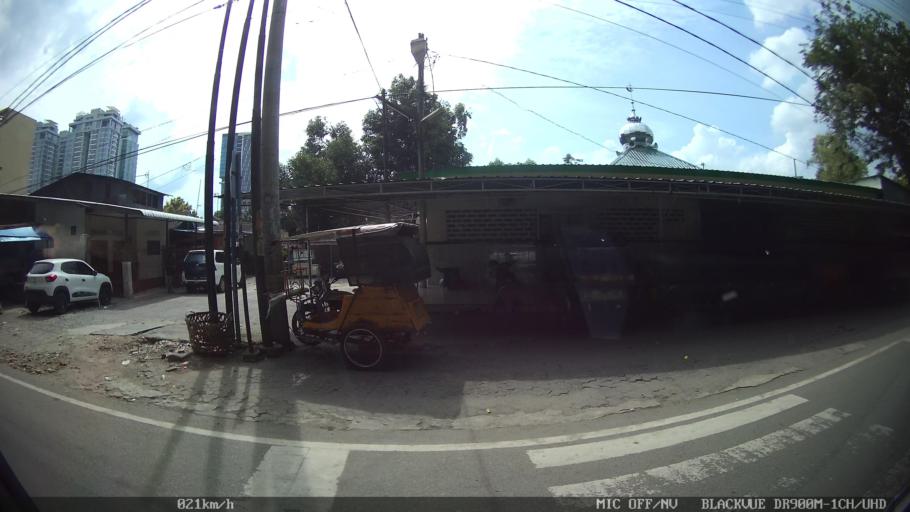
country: ID
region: North Sumatra
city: Medan
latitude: 3.5870
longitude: 98.6706
